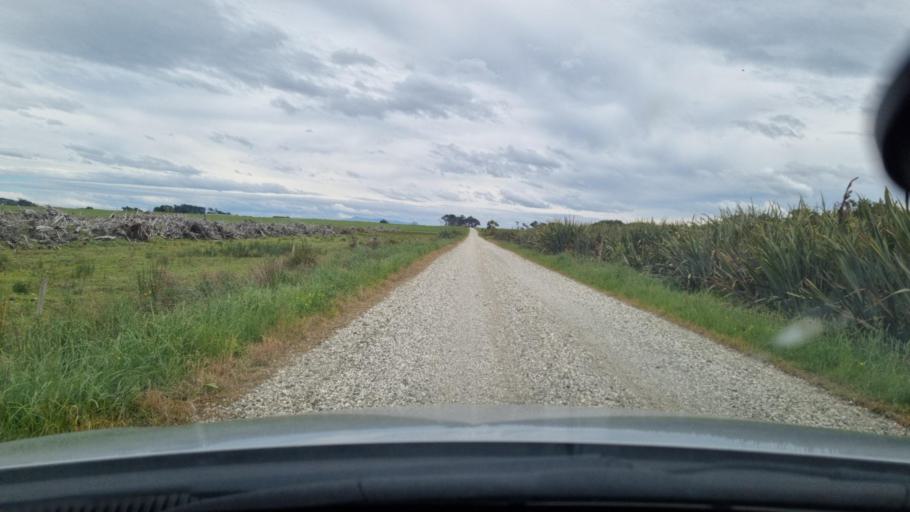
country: NZ
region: Southland
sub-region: Invercargill City
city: Invercargill
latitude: -46.3953
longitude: 168.2689
